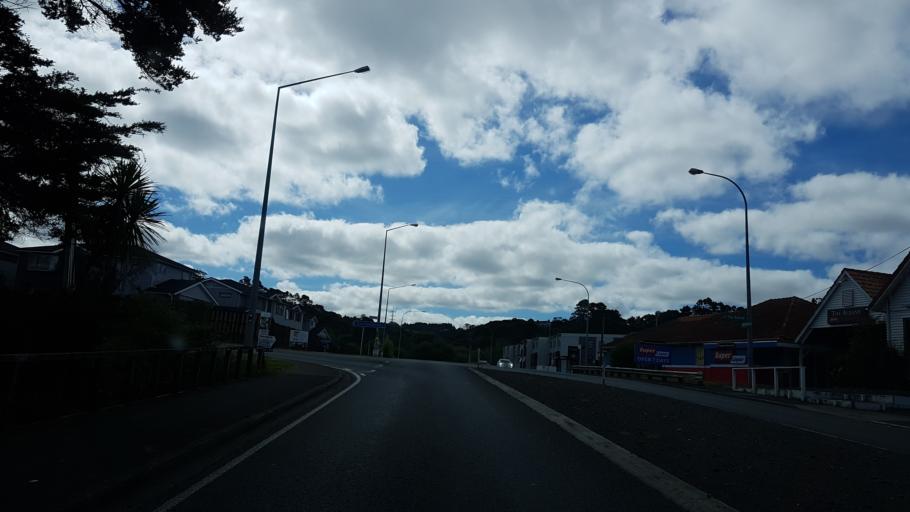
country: NZ
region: Auckland
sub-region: Auckland
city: Rothesay Bay
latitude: -36.7226
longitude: 174.6921
